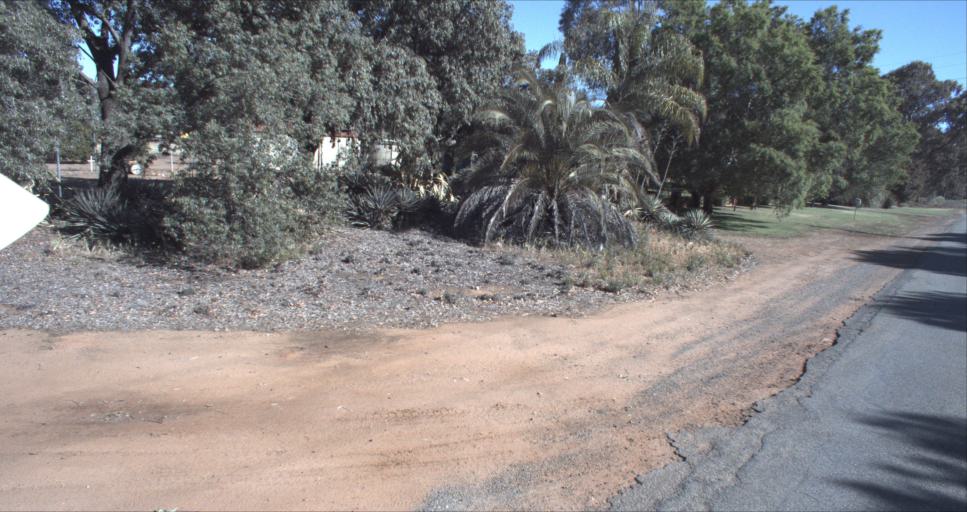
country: AU
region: New South Wales
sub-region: Leeton
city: Leeton
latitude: -34.5754
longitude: 146.3098
